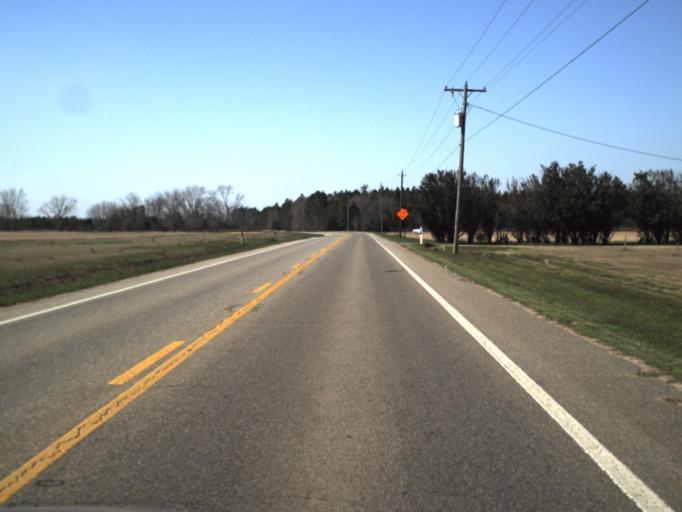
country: US
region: Florida
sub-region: Calhoun County
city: Blountstown
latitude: 30.6015
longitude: -85.1394
